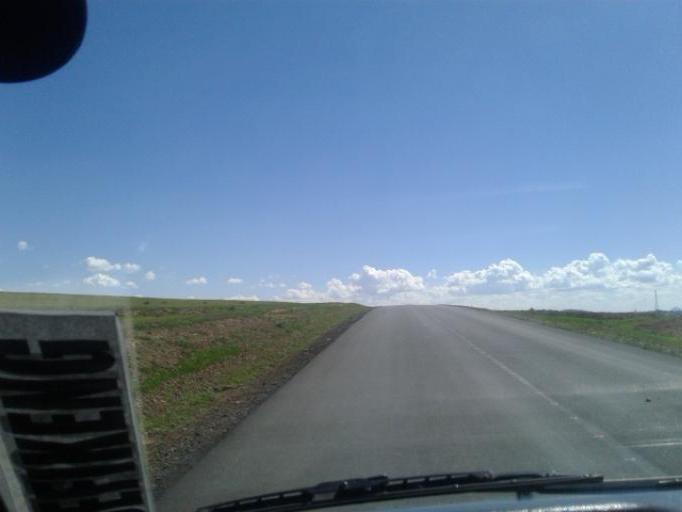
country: LS
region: Maseru
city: Maseru
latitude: -29.3079
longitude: 27.6034
